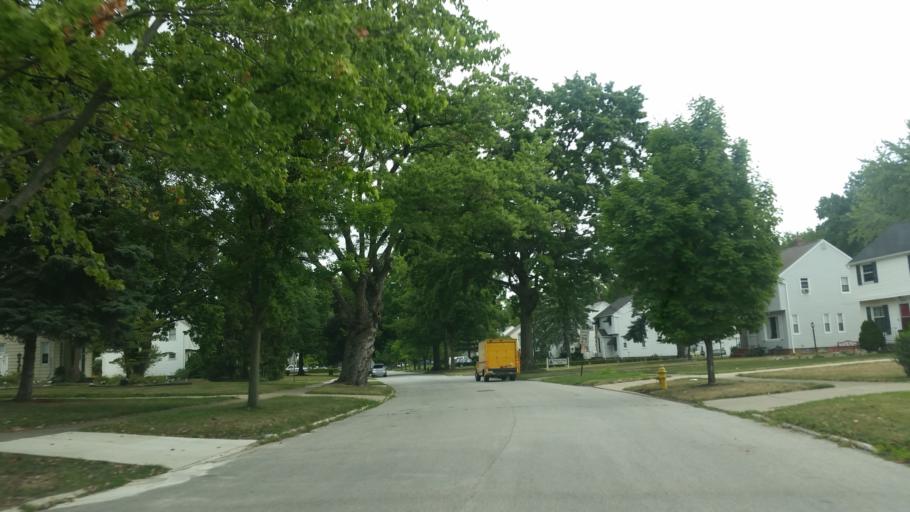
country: US
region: Ohio
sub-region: Cuyahoga County
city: Parma Heights
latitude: 41.3708
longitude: -81.7761
